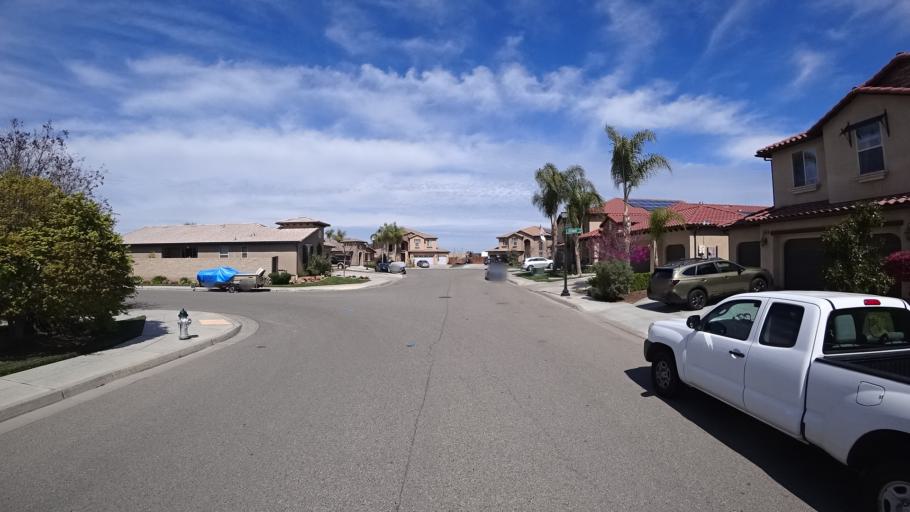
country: US
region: California
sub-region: Fresno County
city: Biola
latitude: 36.8243
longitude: -119.9107
